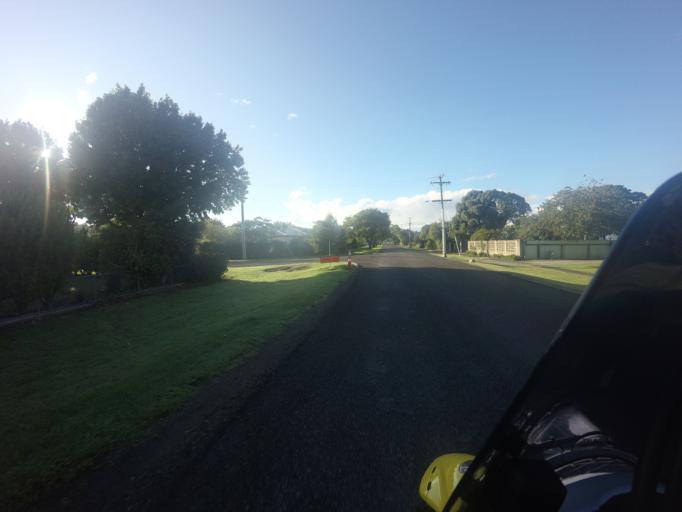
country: NZ
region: Gisborne
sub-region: Gisborne District
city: Gisborne
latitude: -38.6664
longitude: 178.0475
